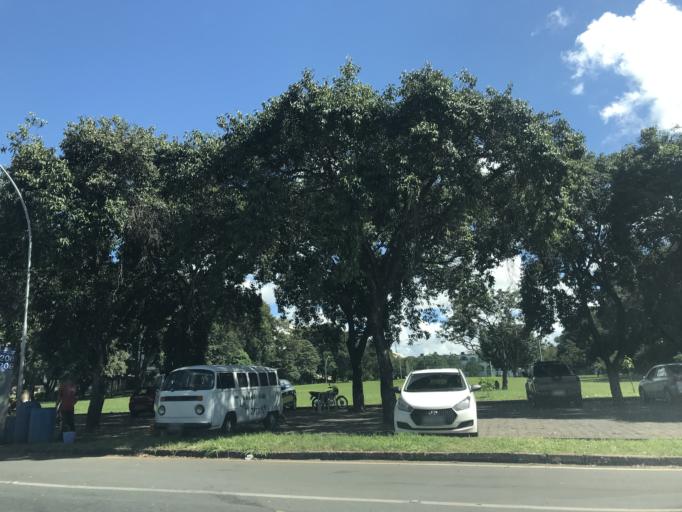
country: BR
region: Federal District
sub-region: Brasilia
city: Brasilia
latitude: -15.8218
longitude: -47.9018
